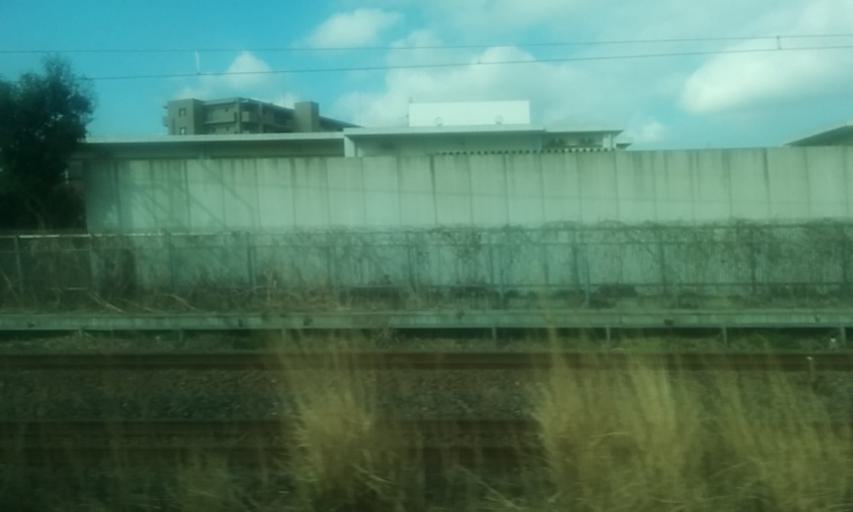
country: JP
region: Kanagawa
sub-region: Kawasaki-shi
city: Kawasaki
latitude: 35.5310
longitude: 139.6783
